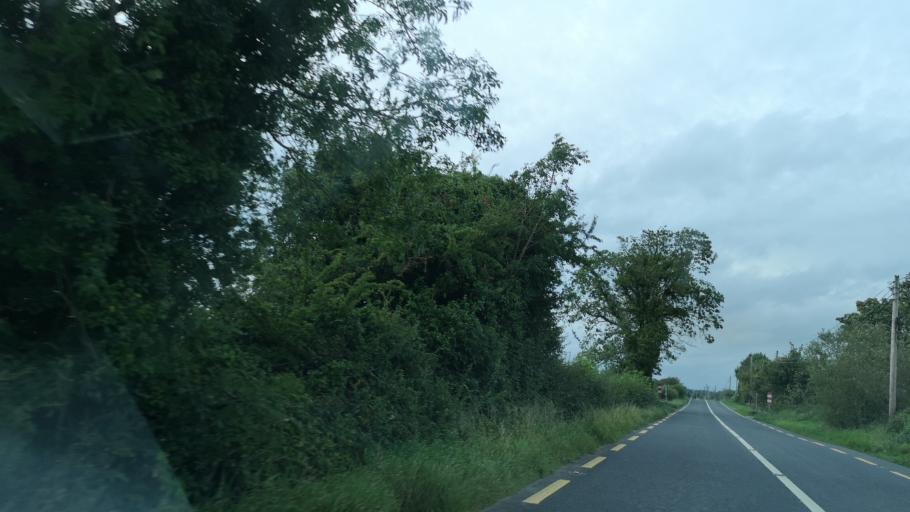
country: IE
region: Leinster
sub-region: Uibh Fhaili
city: Ferbane
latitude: 53.3643
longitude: -7.8534
